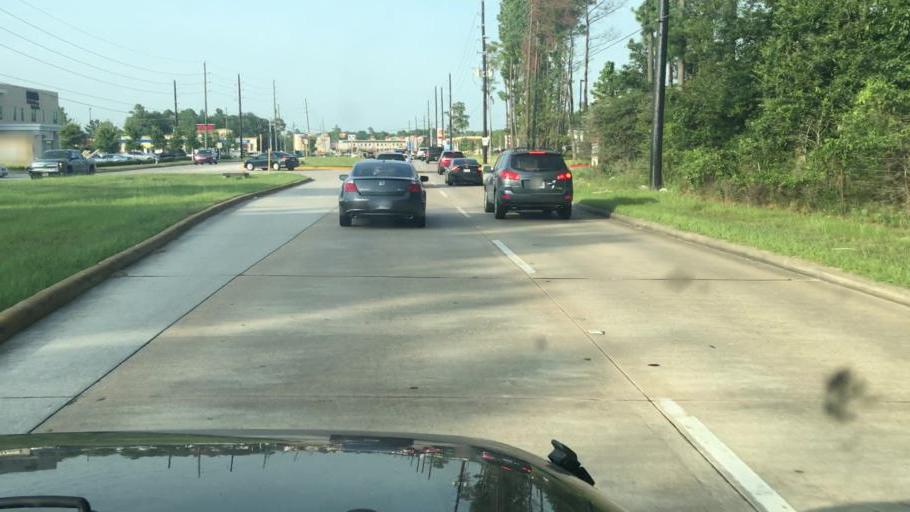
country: US
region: Texas
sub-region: Harris County
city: Atascocita
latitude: 29.9790
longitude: -95.1668
